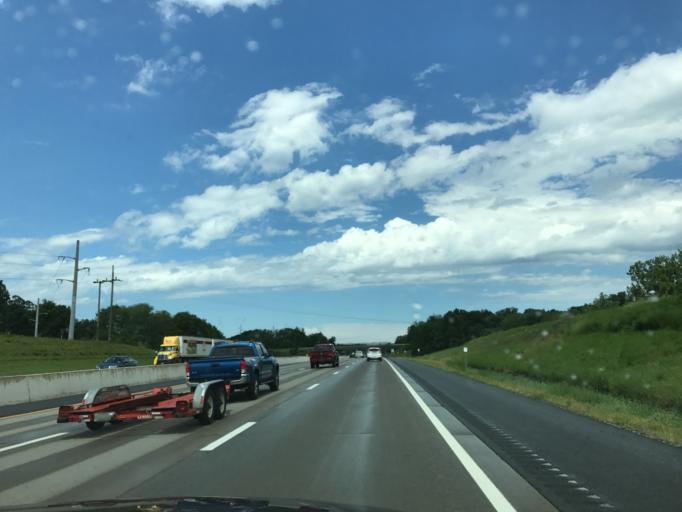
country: US
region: New York
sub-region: Albany County
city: Delmar
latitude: 42.6552
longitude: -73.8205
